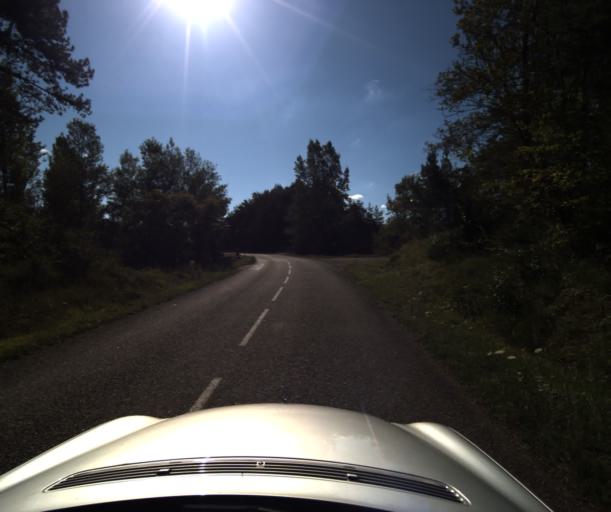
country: FR
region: Languedoc-Roussillon
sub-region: Departement de l'Aude
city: Chalabre
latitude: 42.9677
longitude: 1.9500
